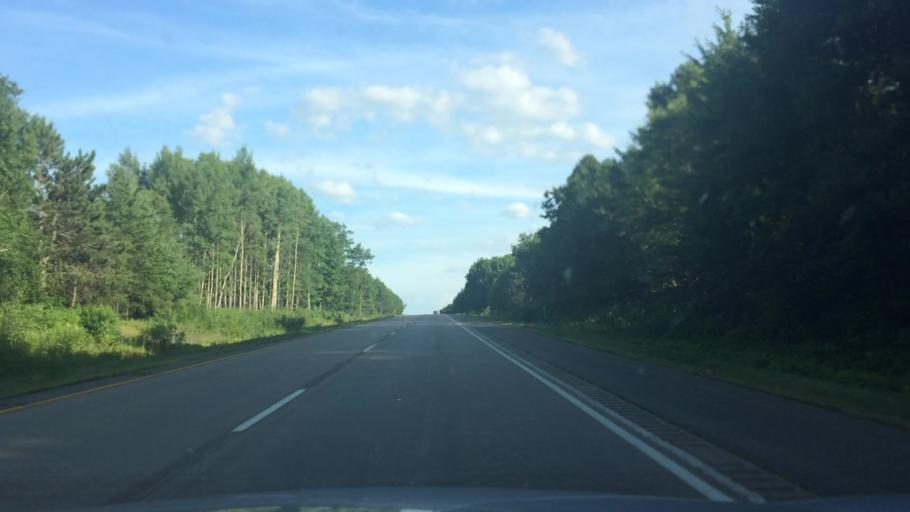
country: US
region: Wisconsin
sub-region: Marathon County
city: Mosinee
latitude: 44.7083
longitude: -89.6566
